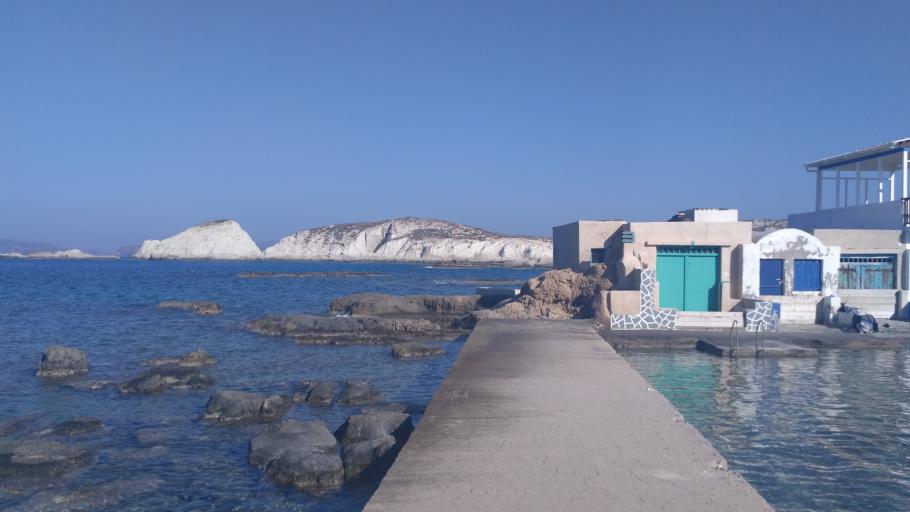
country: GR
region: South Aegean
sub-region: Nomos Kykladon
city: Milos
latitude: 36.7515
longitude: 24.4462
